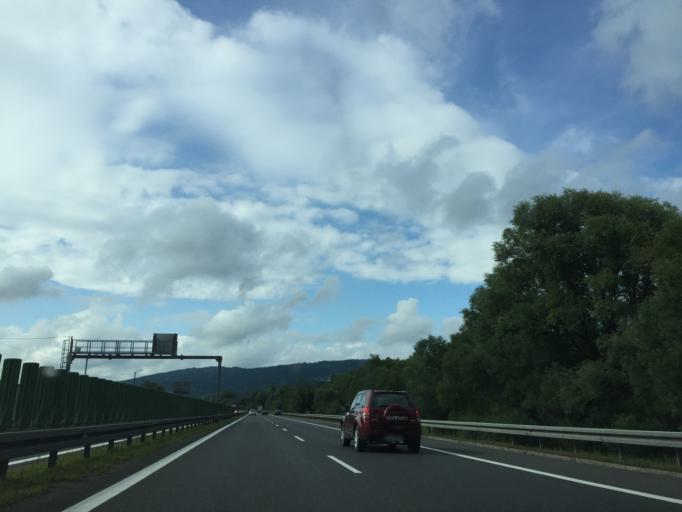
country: PL
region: Lesser Poland Voivodeship
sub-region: Powiat myslenicki
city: Pcim
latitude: 49.7579
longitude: 19.9673
